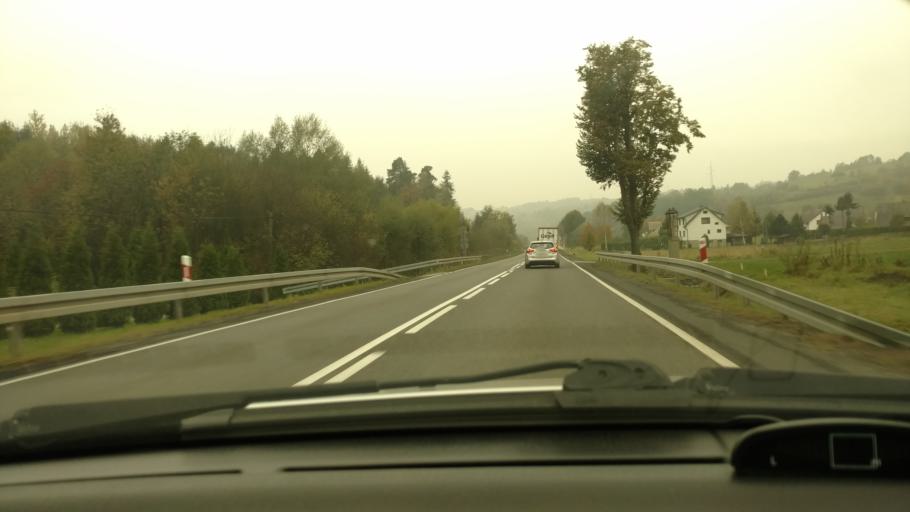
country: PL
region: Lesser Poland Voivodeship
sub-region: Powiat nowosadecki
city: Kamionka Wielka
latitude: 49.6191
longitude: 20.7930
